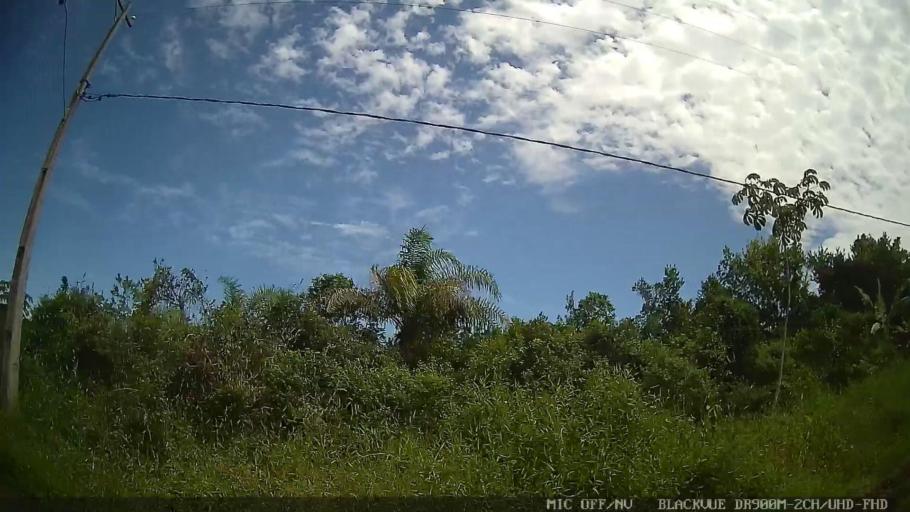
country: BR
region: Sao Paulo
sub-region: Iguape
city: Iguape
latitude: -24.7181
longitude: -47.5347
